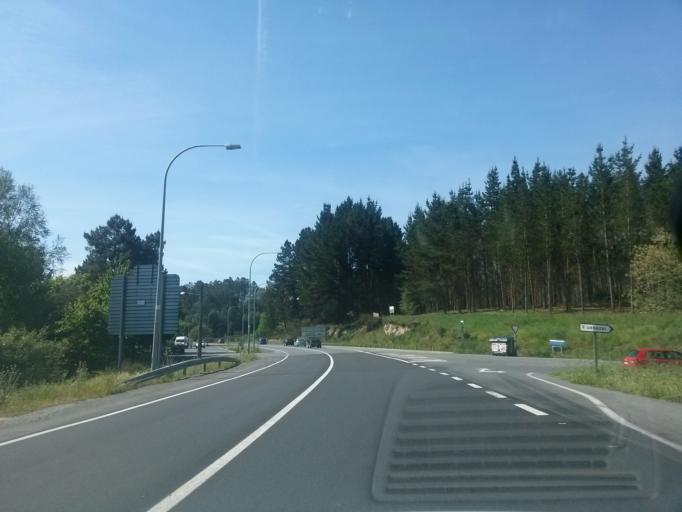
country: ES
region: Galicia
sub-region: Provincia de Lugo
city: Lugo
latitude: 43.0047
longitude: -7.5828
